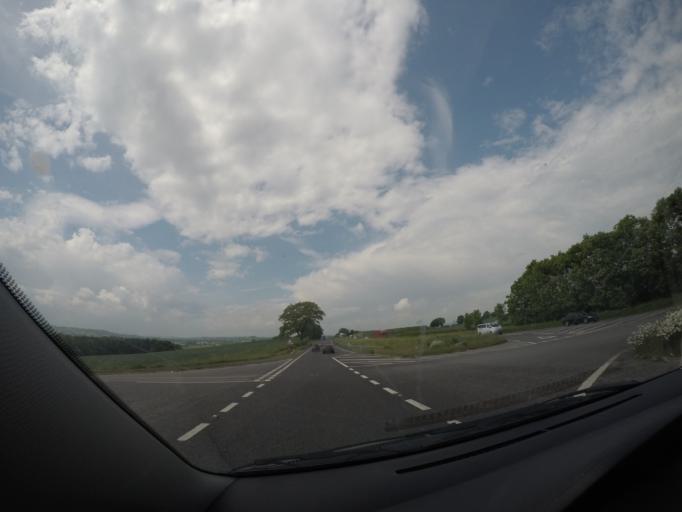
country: GB
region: England
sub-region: County Durham
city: Hutton Magna
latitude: 54.4900
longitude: -1.8091
